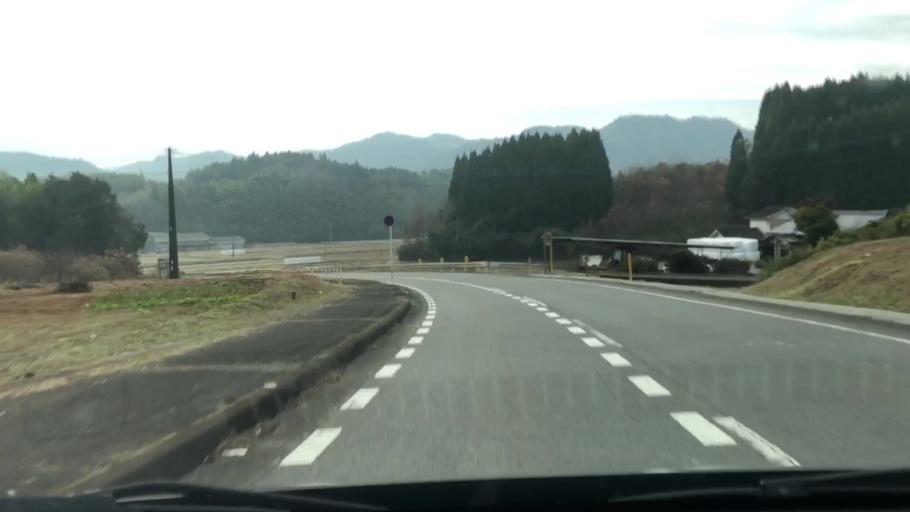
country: JP
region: Oita
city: Takedamachi
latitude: 32.9757
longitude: 131.5595
